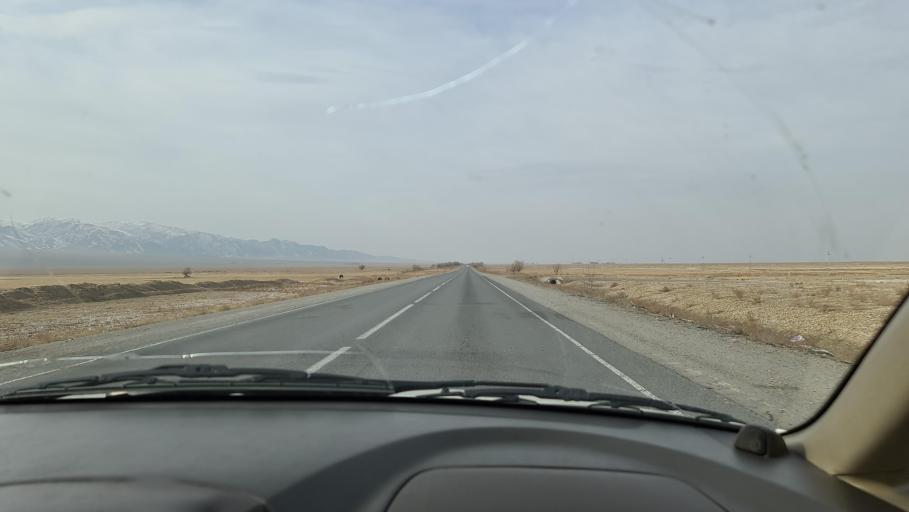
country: KG
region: Chuy
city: Tokmok
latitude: 43.3567
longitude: 75.4197
